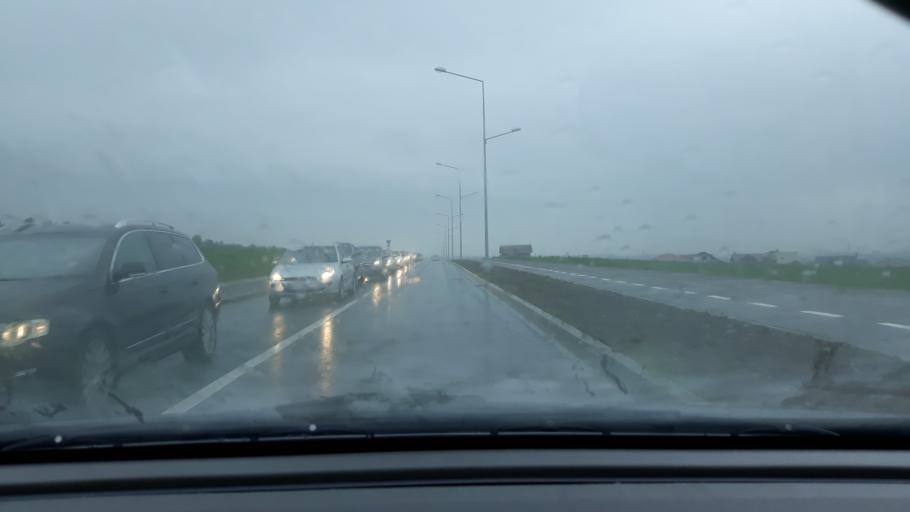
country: RO
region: Bihor
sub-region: Comuna Biharea
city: Biharea
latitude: 47.1085
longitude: 21.9062
